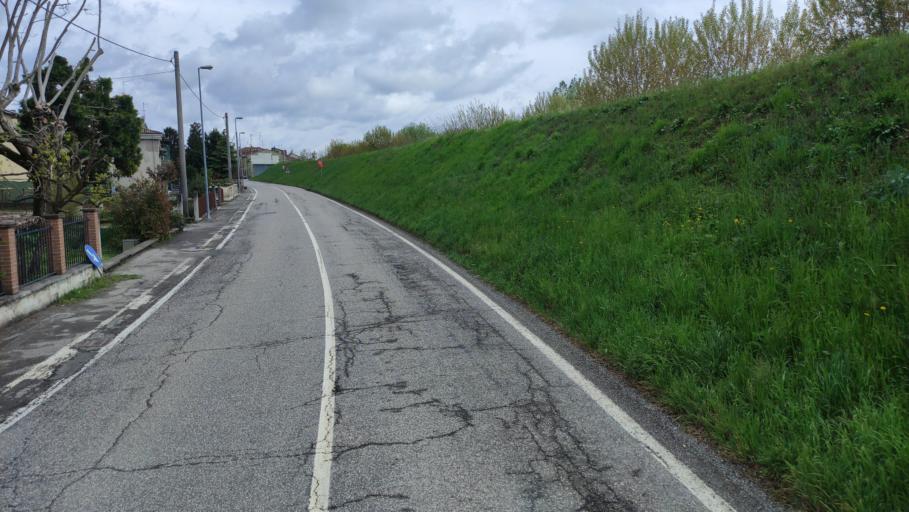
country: IT
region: Emilia-Romagna
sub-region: Provincia di Parma
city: Colorno
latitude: 44.9349
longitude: 10.3642
